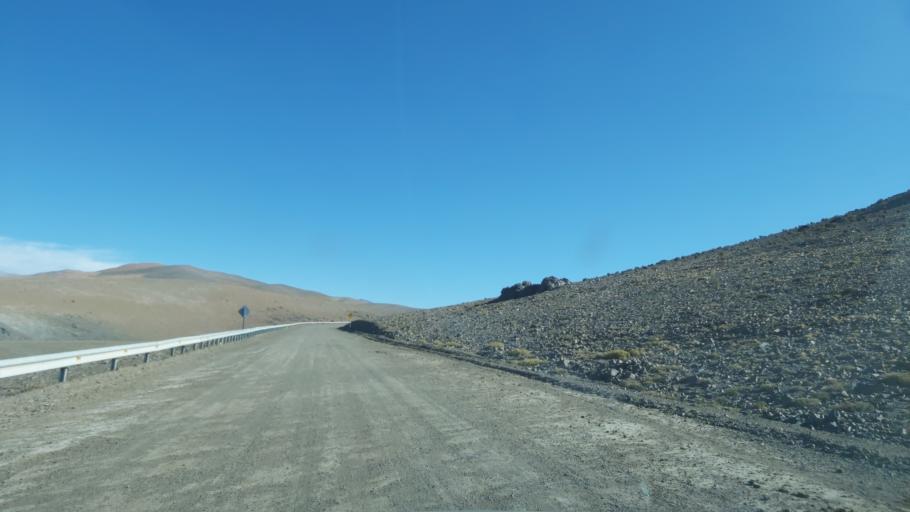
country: CL
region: Atacama
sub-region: Provincia de Chanaral
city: Diego de Almagro
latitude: -26.4272
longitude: -69.2802
